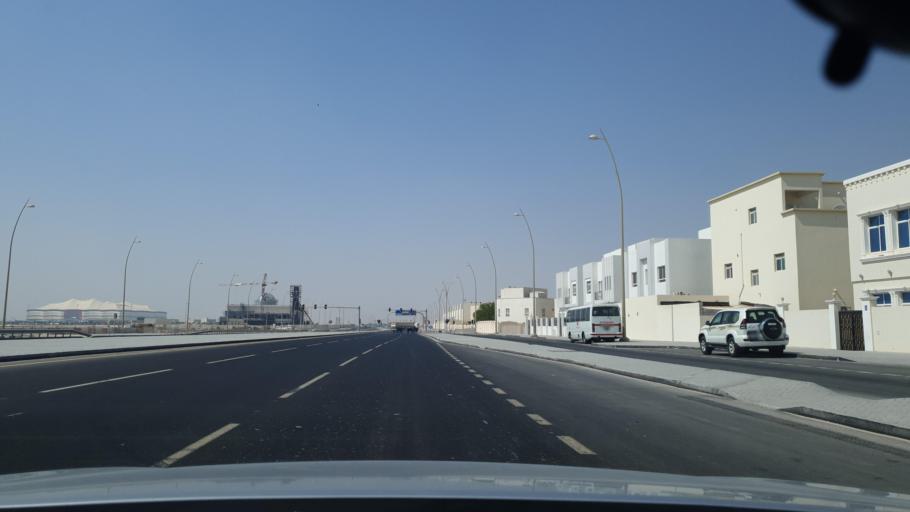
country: QA
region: Al Khawr
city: Al Khawr
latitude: 25.6653
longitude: 51.5094
